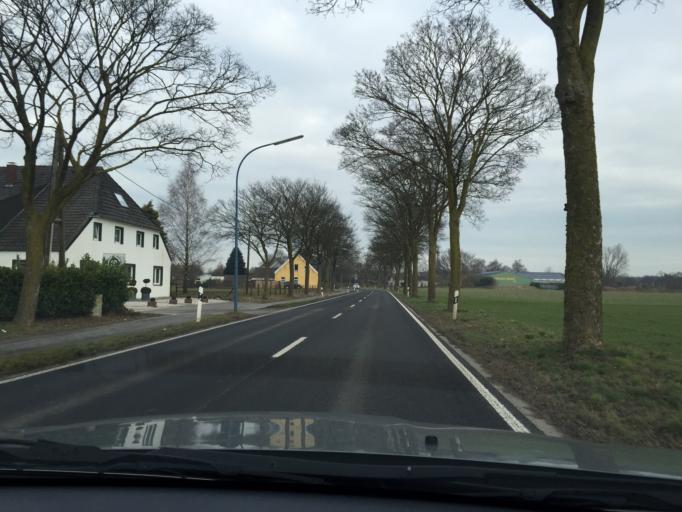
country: DE
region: North Rhine-Westphalia
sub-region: Regierungsbezirk Dusseldorf
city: Kleve
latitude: 51.7646
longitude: 6.1320
